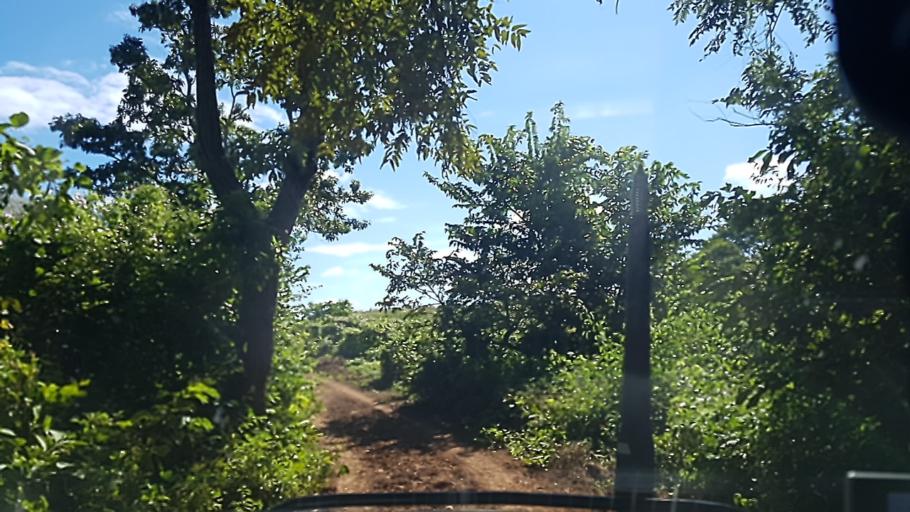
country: NI
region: Granada
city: Nandaime
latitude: 11.5698
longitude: -86.0908
